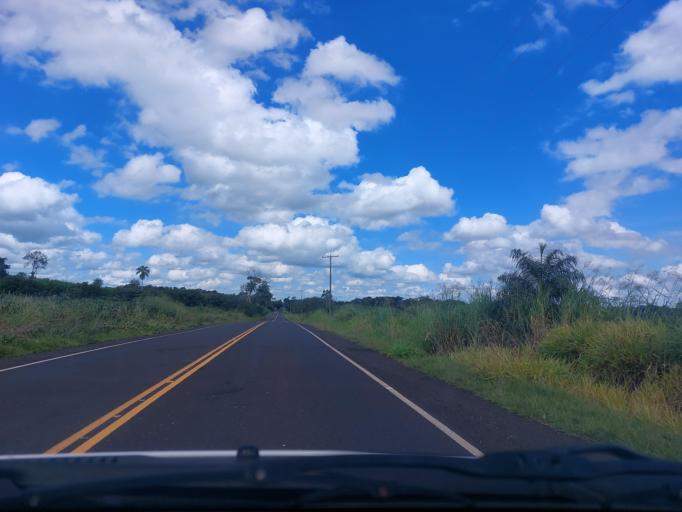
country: PY
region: San Pedro
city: Guayaybi
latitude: -24.5607
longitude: -56.5195
